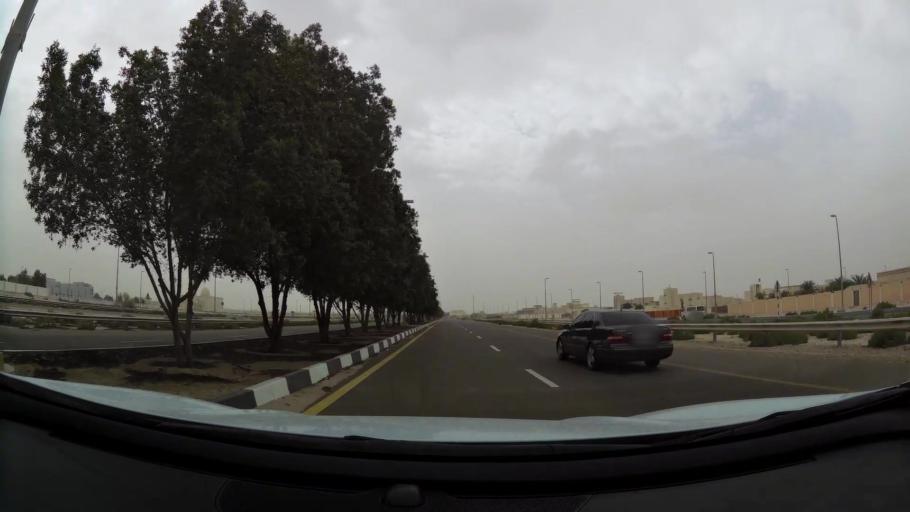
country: AE
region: Abu Dhabi
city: Abu Dhabi
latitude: 24.3842
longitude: 54.7055
